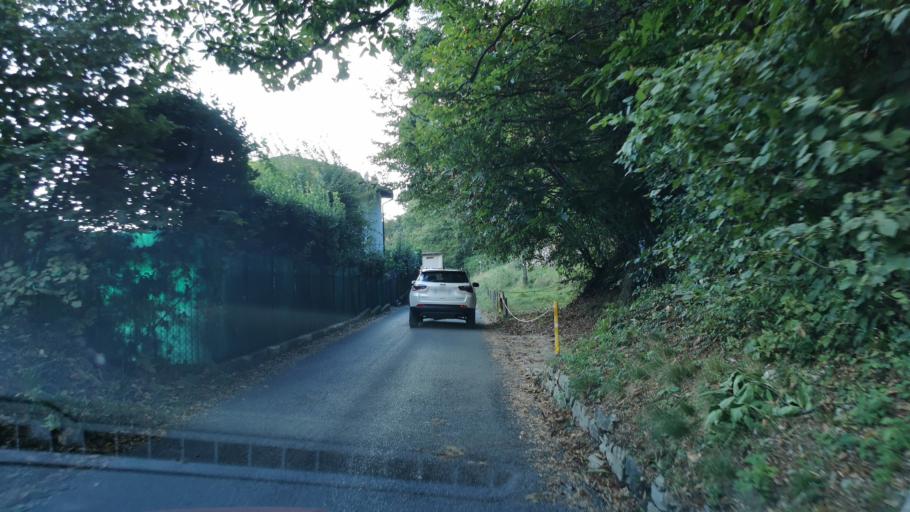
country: IT
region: Lombardy
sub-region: Provincia di Como
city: Cernobbio
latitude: 45.8536
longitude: 9.0831
